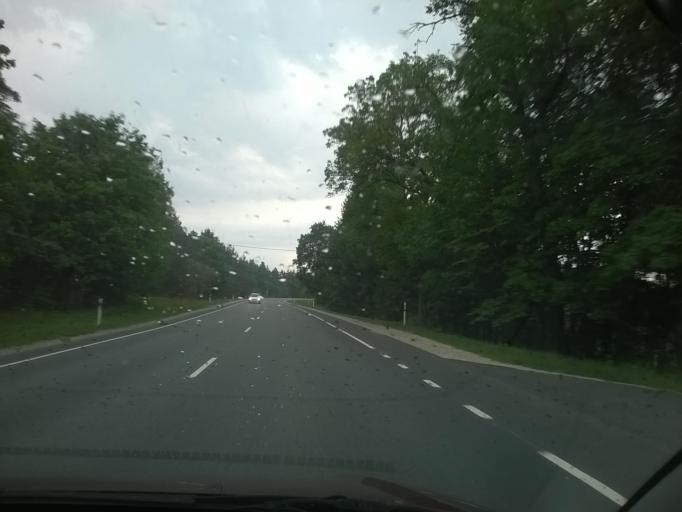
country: EE
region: Harju
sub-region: Nissi vald
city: Turba
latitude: 59.0401
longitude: 24.1679
